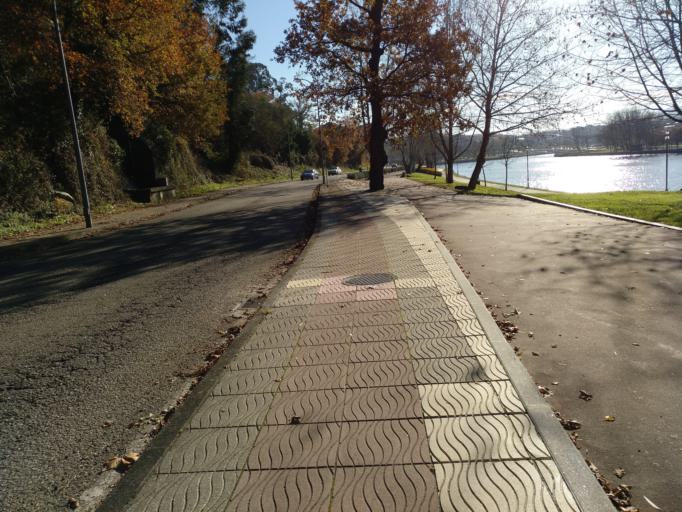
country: ES
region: Galicia
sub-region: Provincia de Pontevedra
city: Pontevedra
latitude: 42.4421
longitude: -8.6324
